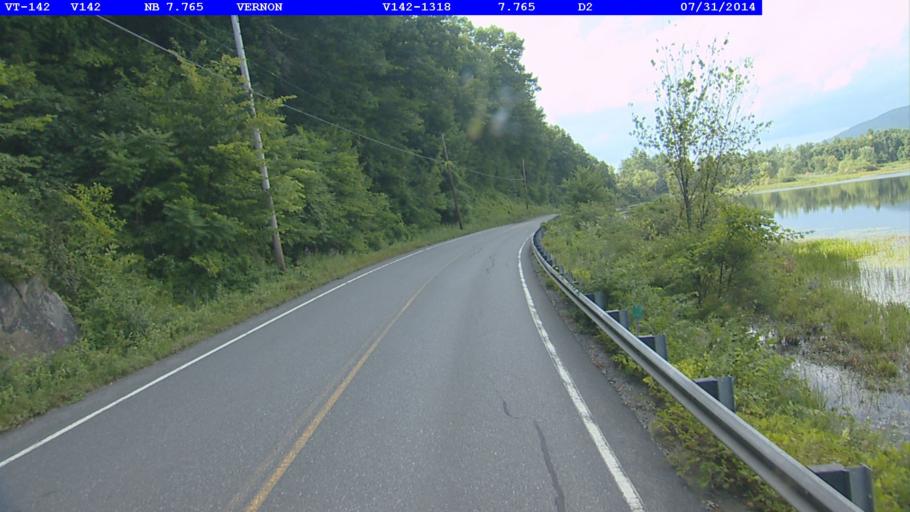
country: US
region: Vermont
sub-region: Windham County
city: Brattleboro
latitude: 42.8120
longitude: -72.5456
